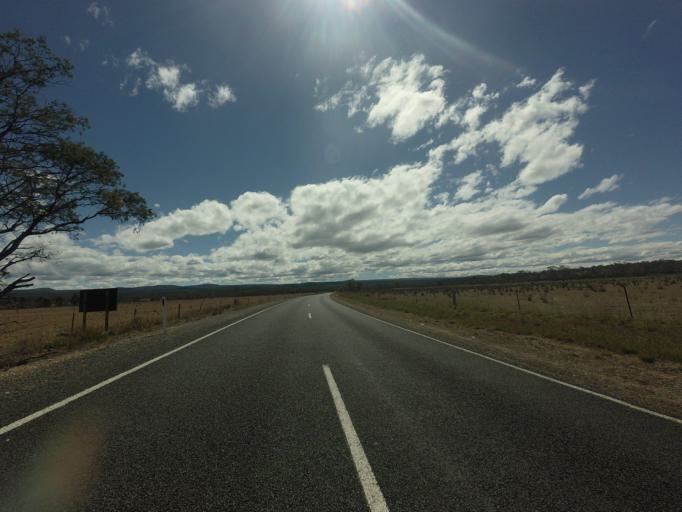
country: AU
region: Tasmania
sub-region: Break O'Day
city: St Helens
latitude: -42.0453
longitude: 148.0392
